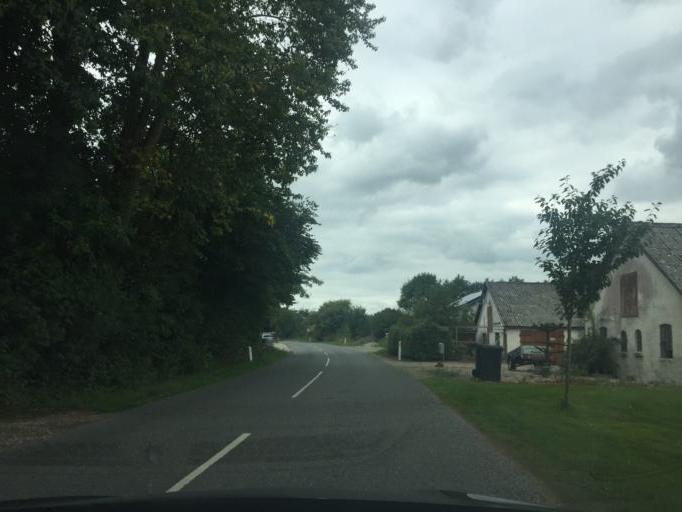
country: DK
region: South Denmark
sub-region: Assens Kommune
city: Tommerup
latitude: 55.3566
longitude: 10.2142
